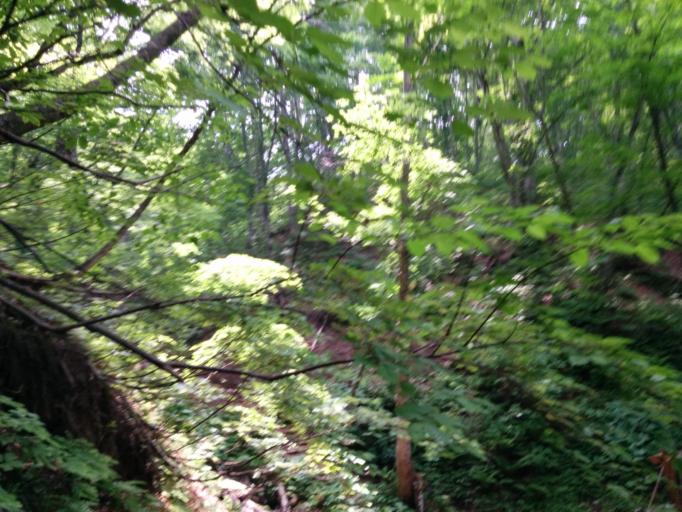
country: JP
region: Aomori
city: Hirosaki
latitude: 40.5203
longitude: 140.1693
